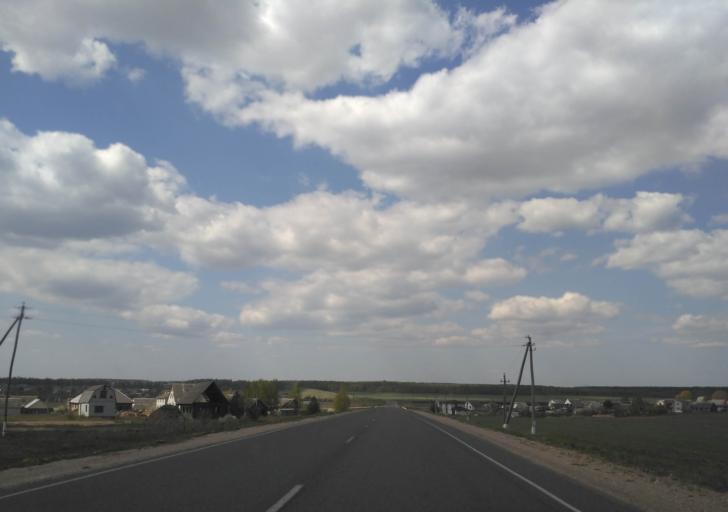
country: BY
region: Minsk
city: Vilyeyka
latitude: 54.5167
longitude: 26.9817
